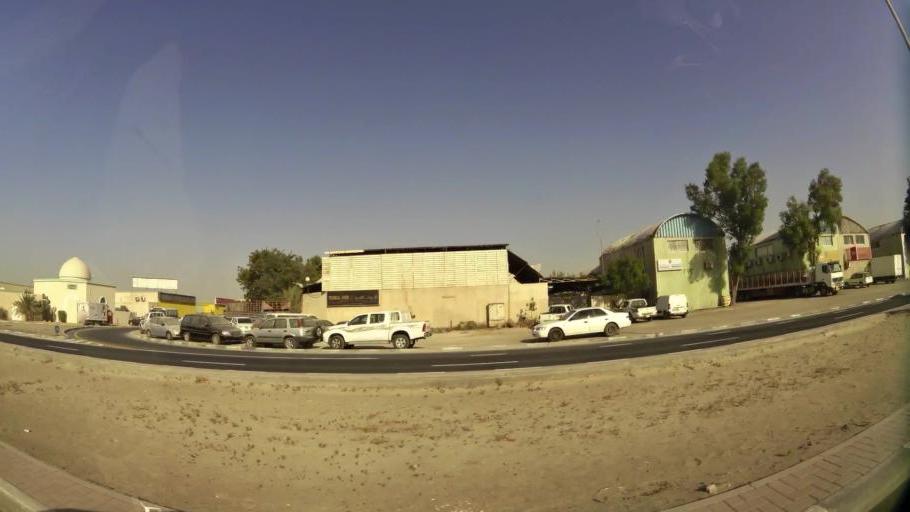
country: AE
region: Ash Shariqah
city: Sharjah
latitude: 25.2865
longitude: 55.3819
